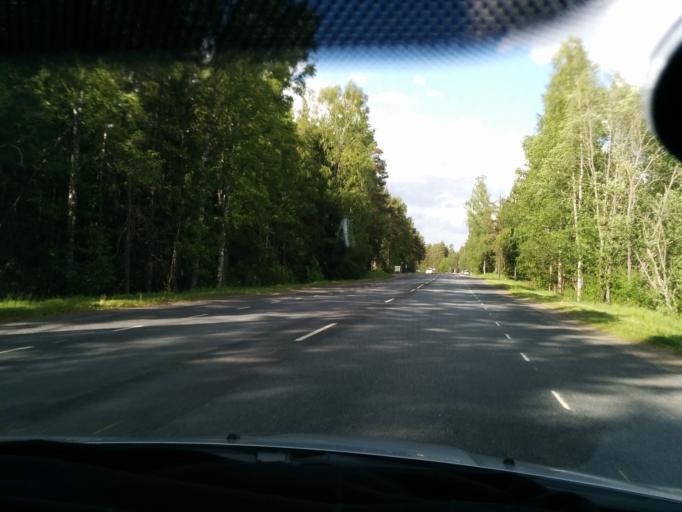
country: EE
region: Harju
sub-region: Loksa linn
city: Loksa
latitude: 59.5388
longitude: 25.7332
